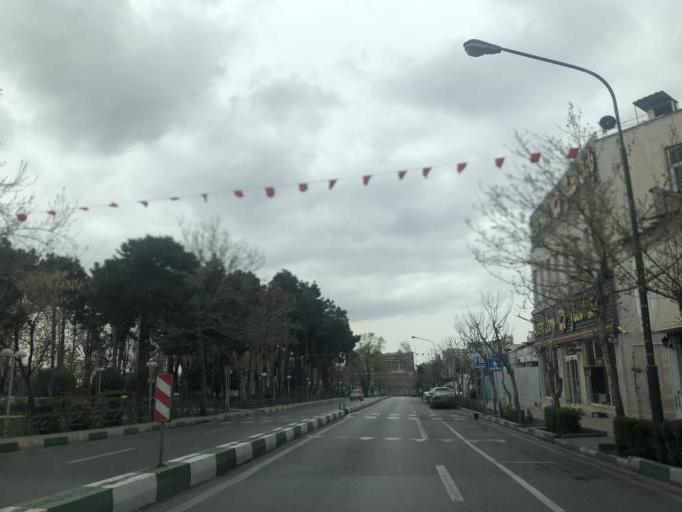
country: IR
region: Tehran
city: Tajrish
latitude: 35.7801
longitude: 51.4675
